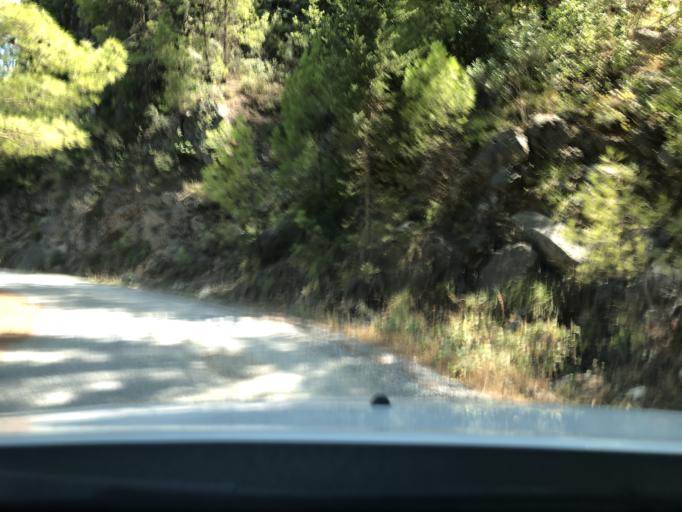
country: TR
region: Antalya
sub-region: Manavgat
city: Manavgat
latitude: 36.9069
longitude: 31.5559
